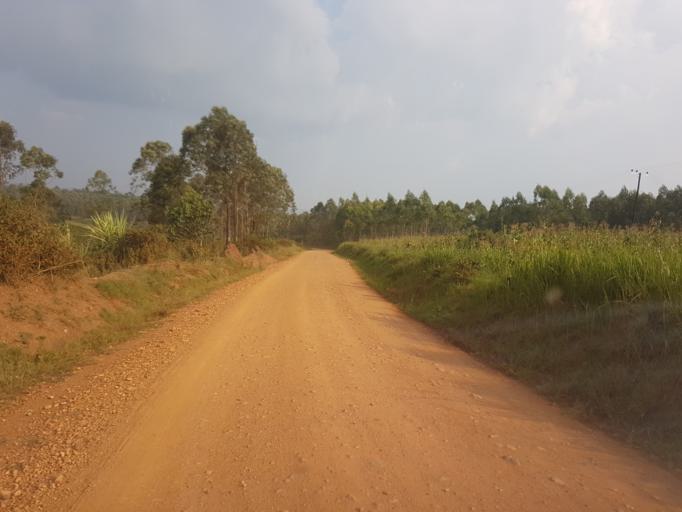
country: UG
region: Western Region
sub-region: Rukungiri District
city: Rukungiri
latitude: -0.6604
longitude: 29.8641
